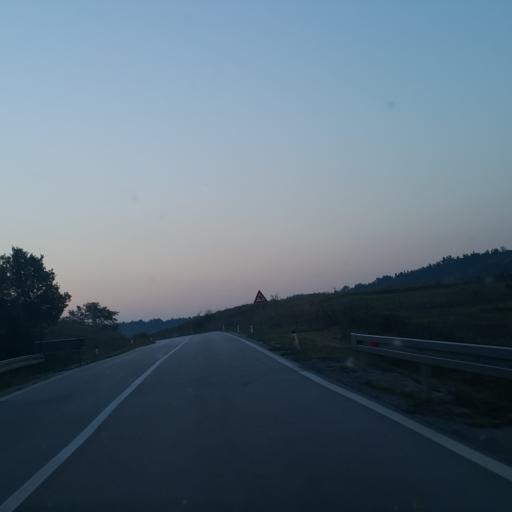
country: RS
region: Central Serbia
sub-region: Nisavski Okrug
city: Svrljig
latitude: 43.4537
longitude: 22.1880
